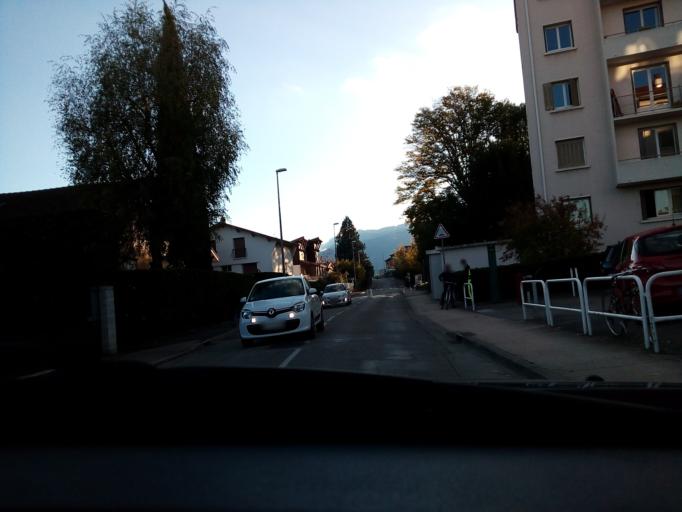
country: FR
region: Rhone-Alpes
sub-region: Departement de l'Isere
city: La Tronche
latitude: 45.2013
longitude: 5.7519
